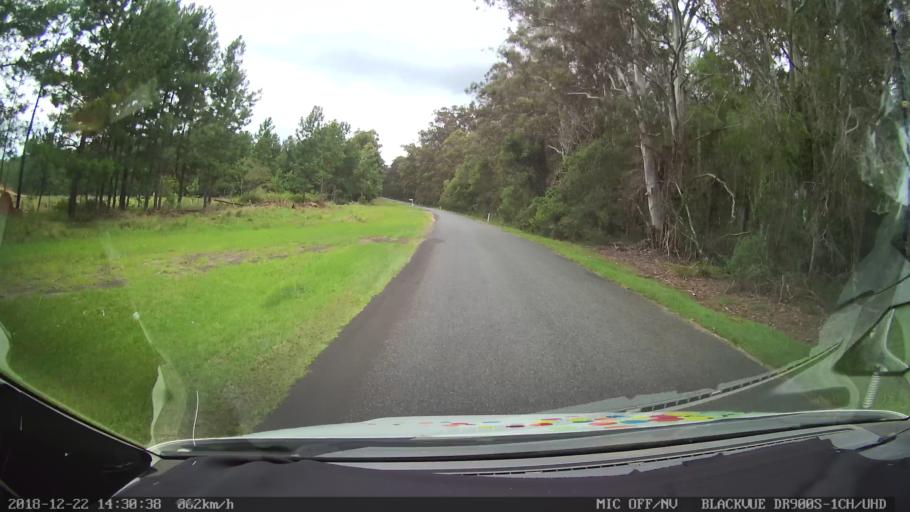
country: AU
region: New South Wales
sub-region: Bellingen
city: Dorrigo
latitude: -30.0886
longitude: 152.6313
